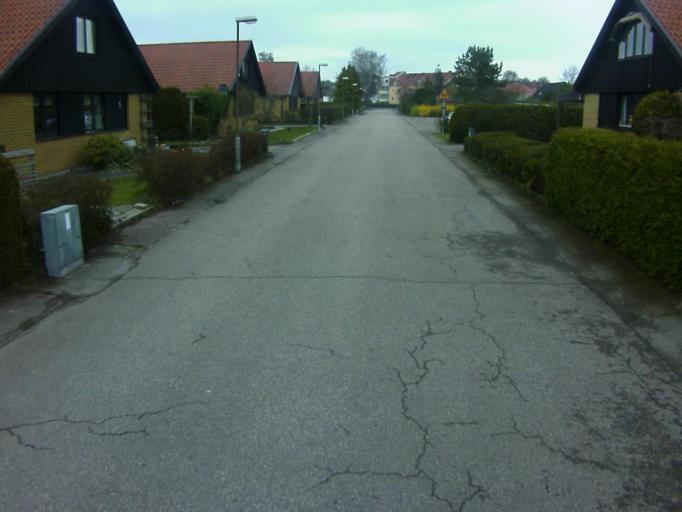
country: SE
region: Skane
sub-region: Kavlinge Kommun
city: Kaevlinge
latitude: 55.7720
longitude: 13.0867
